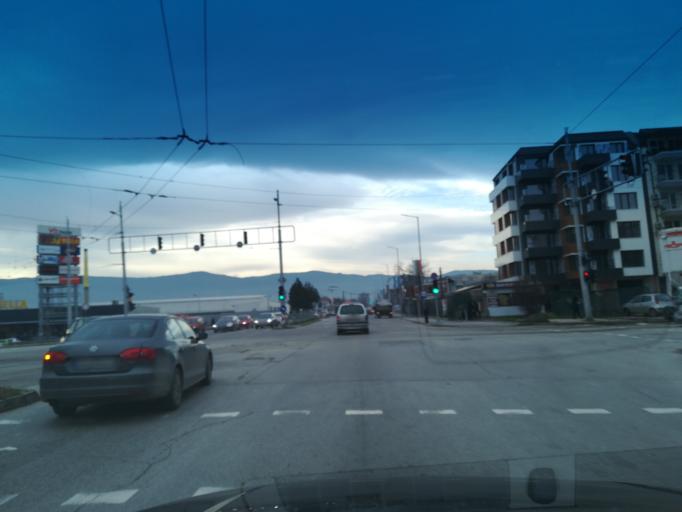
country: BG
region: Plovdiv
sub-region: Obshtina Plovdiv
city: Plovdiv
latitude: 42.1258
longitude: 24.7202
